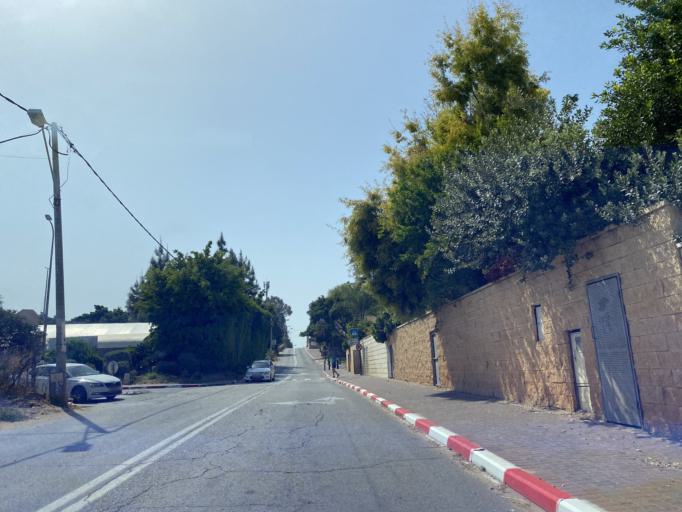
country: IL
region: Central District
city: Ra'anana
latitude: 32.1733
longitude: 34.8761
